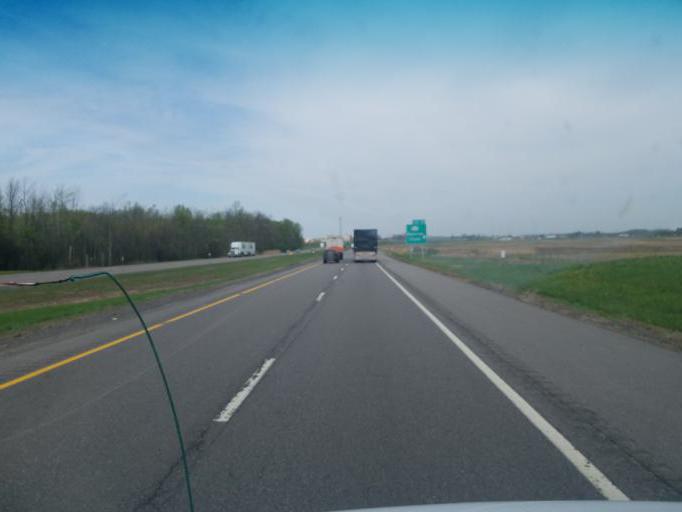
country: US
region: New York
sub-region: Seneca County
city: Waterloo
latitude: 42.9660
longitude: -76.8605
